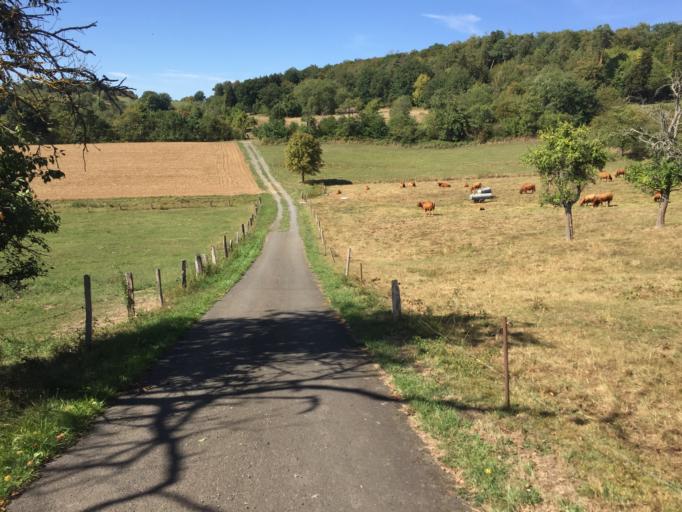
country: DE
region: Hesse
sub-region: Regierungsbezirk Giessen
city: Reiskirchen
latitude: 50.6010
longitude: 8.8886
